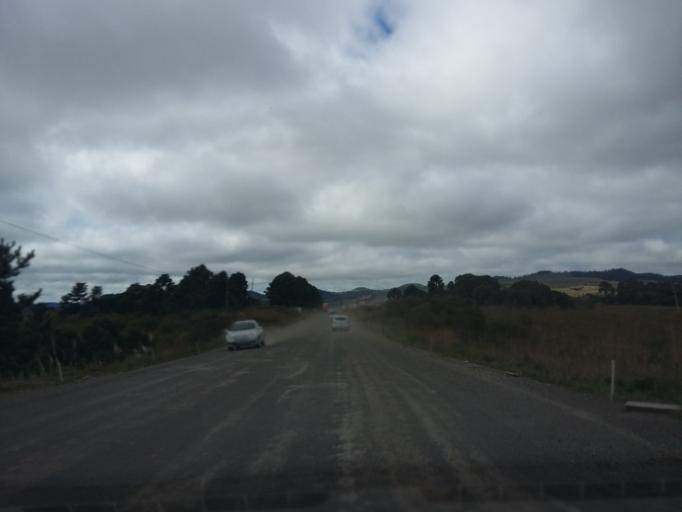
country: BR
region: Santa Catarina
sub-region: Lages
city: Lages
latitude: -27.9102
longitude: -50.1148
